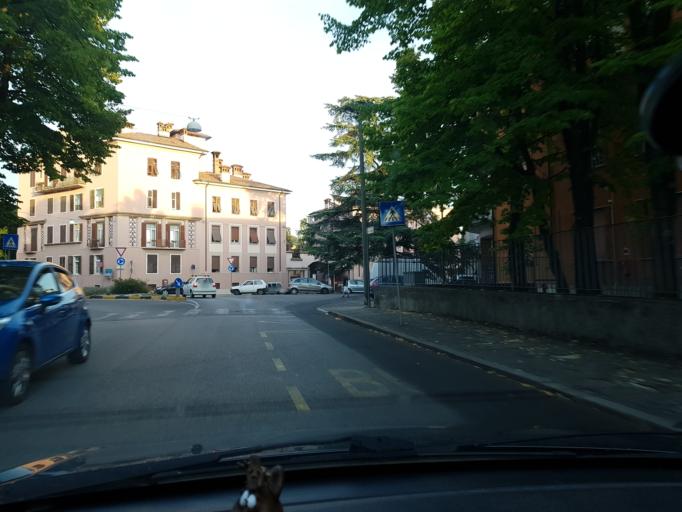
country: IT
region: Friuli Venezia Giulia
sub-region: Provincia di Gorizia
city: Gorizia
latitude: 45.9512
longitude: 13.6277
